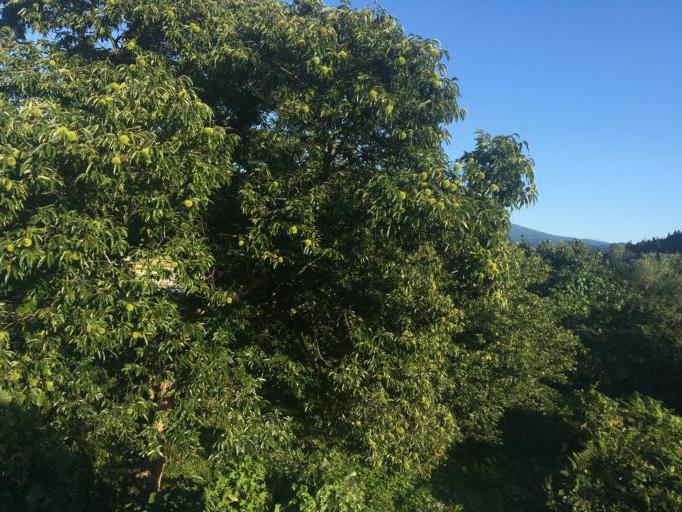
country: JP
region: Akita
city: Takanosu
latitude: 40.0566
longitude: 140.4158
